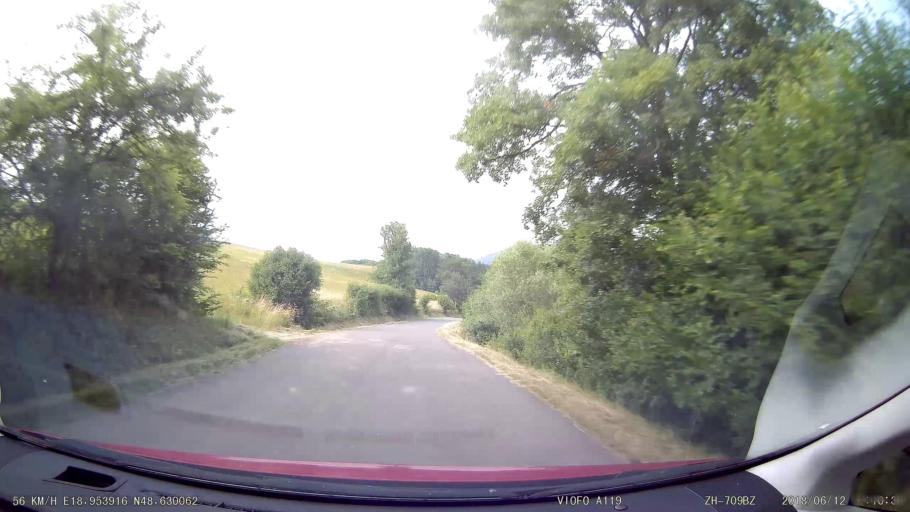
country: SK
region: Banskobystricky
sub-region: Okres Ziar nad Hronom
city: Kremnica
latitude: 48.6303
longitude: 18.9539
